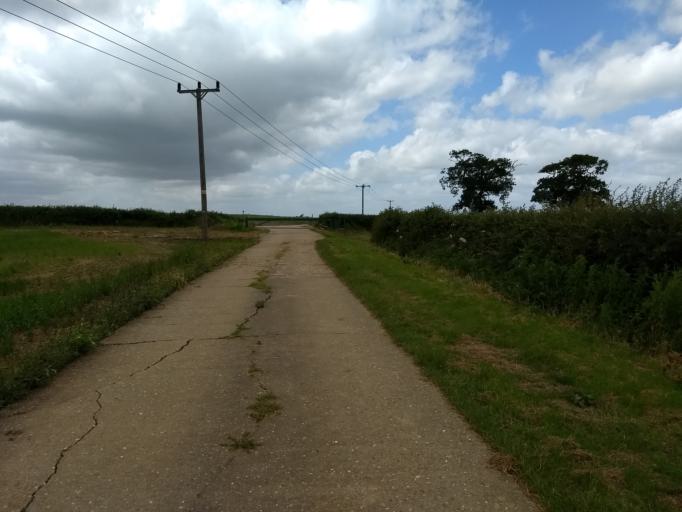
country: GB
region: England
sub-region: Milton Keynes
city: Calverton
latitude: 52.0145
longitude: -0.8326
